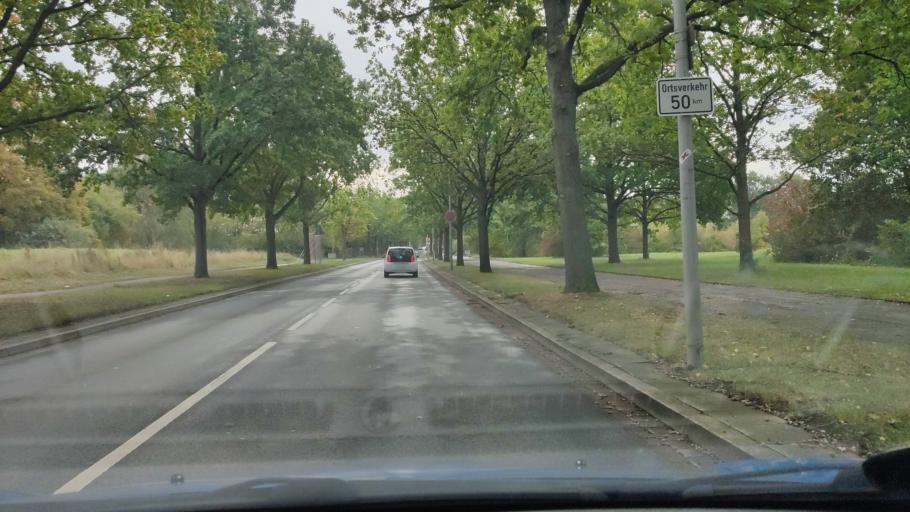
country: DE
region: Lower Saxony
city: Ronnenberg
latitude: 52.3629
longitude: 9.6783
